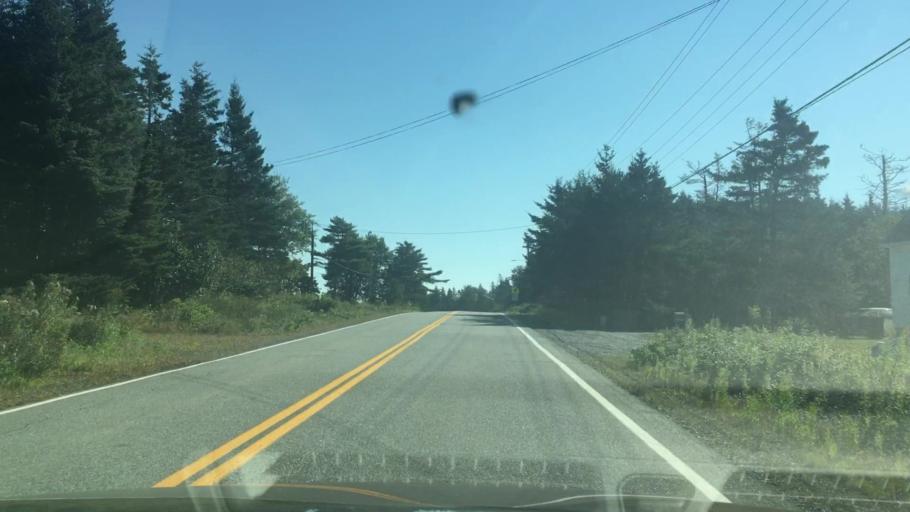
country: CA
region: Nova Scotia
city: New Glasgow
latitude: 44.8036
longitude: -62.7016
